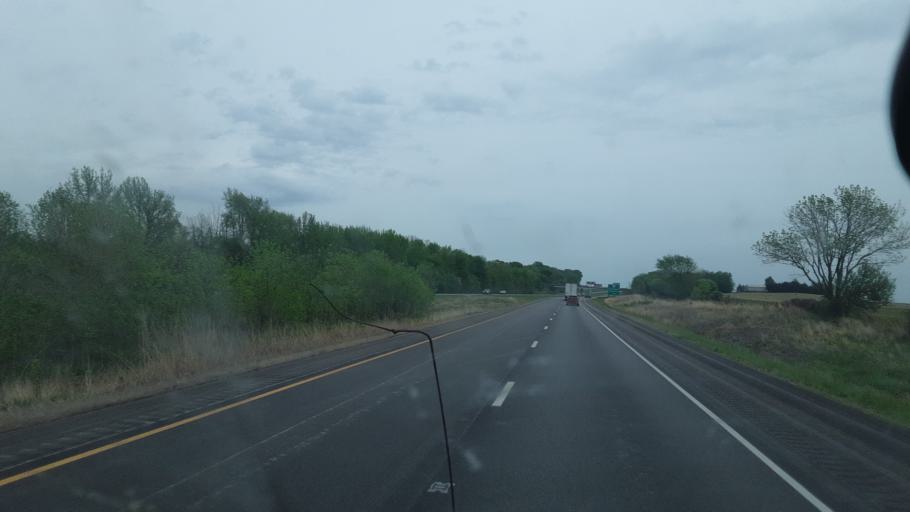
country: US
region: Indiana
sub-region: Posey County
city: Poseyville
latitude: 38.1644
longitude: -87.7133
